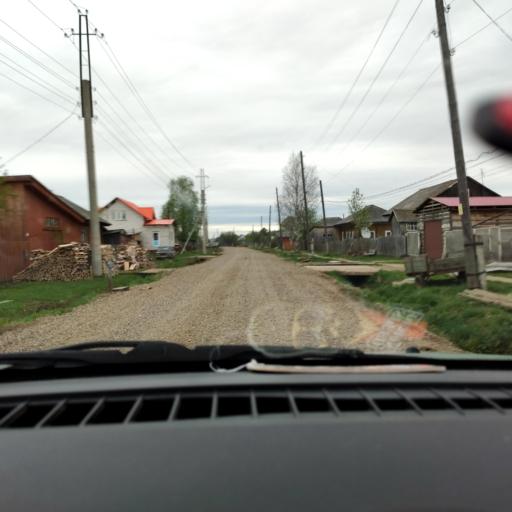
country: RU
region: Perm
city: Kudymkar
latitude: 59.0130
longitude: 54.6271
